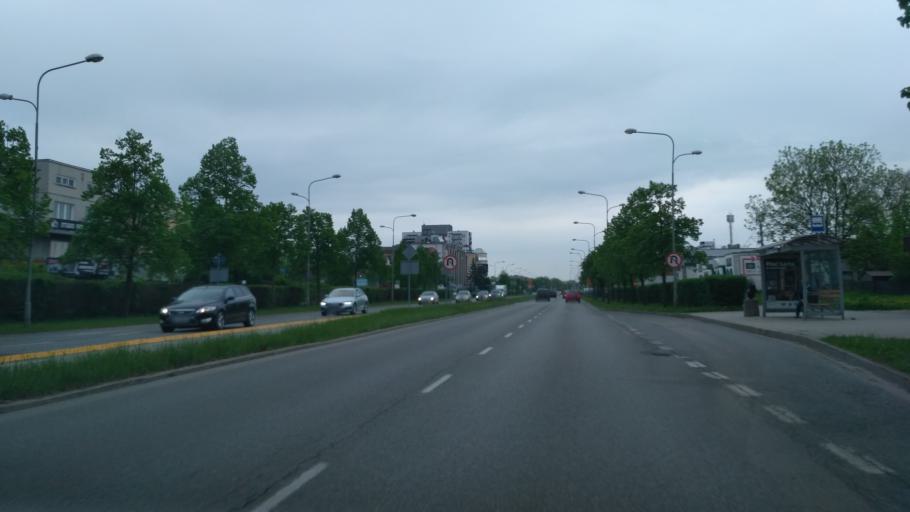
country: PL
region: Lesser Poland Voivodeship
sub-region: Powiat tarnowski
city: Tarnow
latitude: 50.0181
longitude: 20.9971
